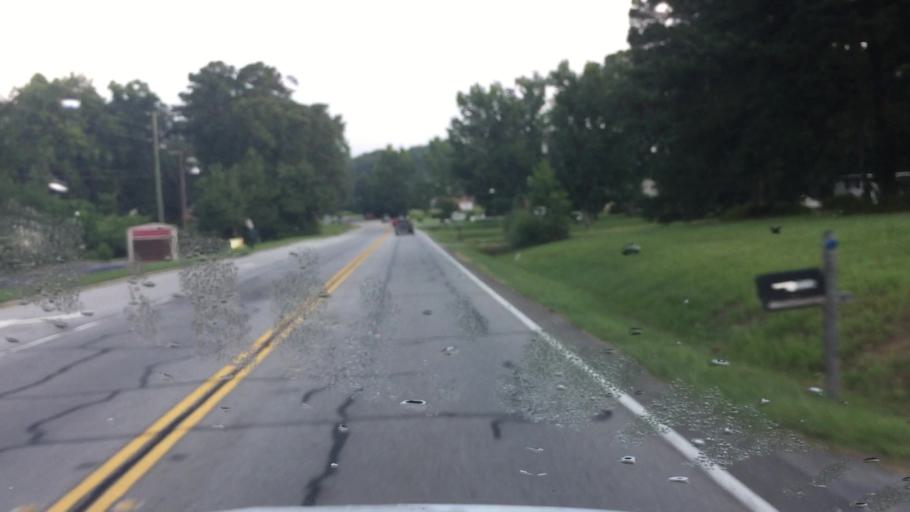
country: US
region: Georgia
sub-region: DeKalb County
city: Pine Mountain
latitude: 33.6054
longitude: -84.1598
